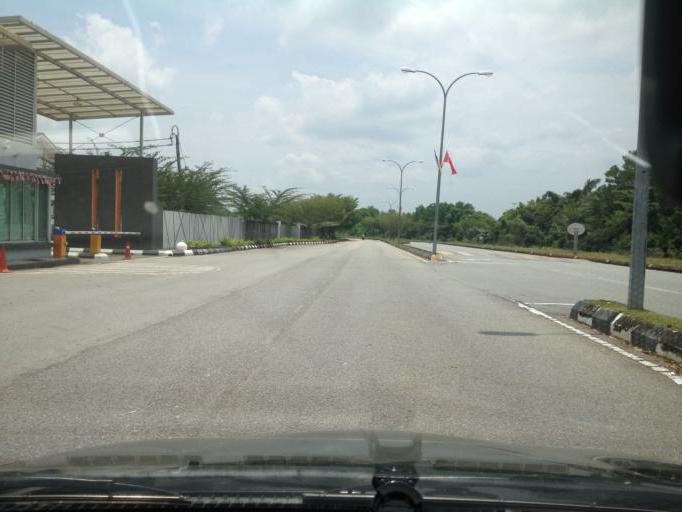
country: MY
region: Kedah
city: Sungai Petani
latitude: 5.6093
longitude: 100.5463
